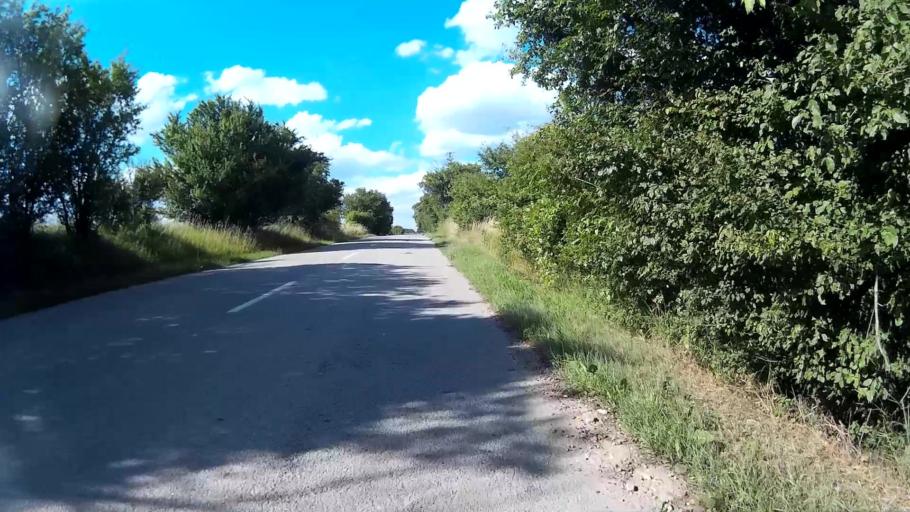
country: CZ
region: South Moravian
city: Sitborice
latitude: 49.0041
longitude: 16.7787
